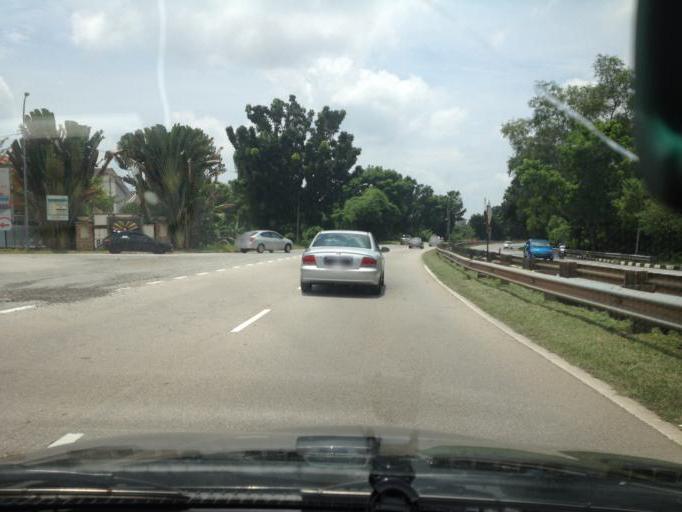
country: MY
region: Kedah
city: Sungai Petani
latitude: 5.6307
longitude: 100.5394
